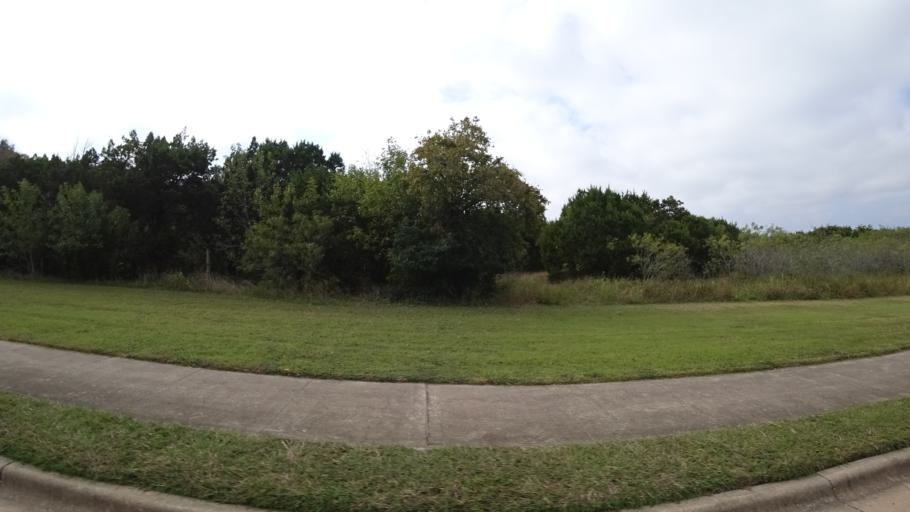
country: US
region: Texas
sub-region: Travis County
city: Shady Hollow
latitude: 30.2095
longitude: -97.8211
